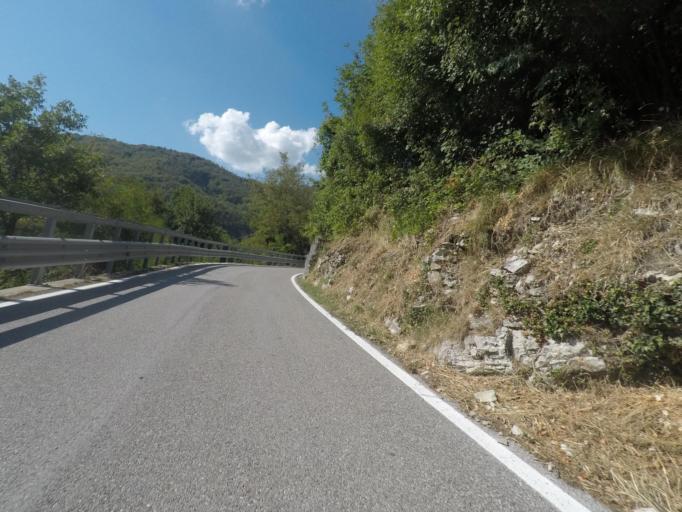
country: IT
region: Tuscany
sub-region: Provincia di Massa-Carrara
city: Fivizzano
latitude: 44.2525
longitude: 10.1740
